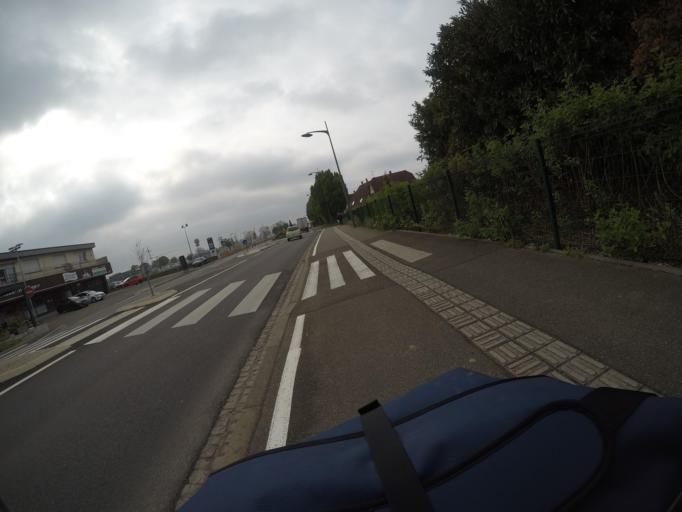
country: FR
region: Alsace
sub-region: Departement du Bas-Rhin
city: Mittelhausbergen
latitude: 48.6136
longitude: 7.6958
